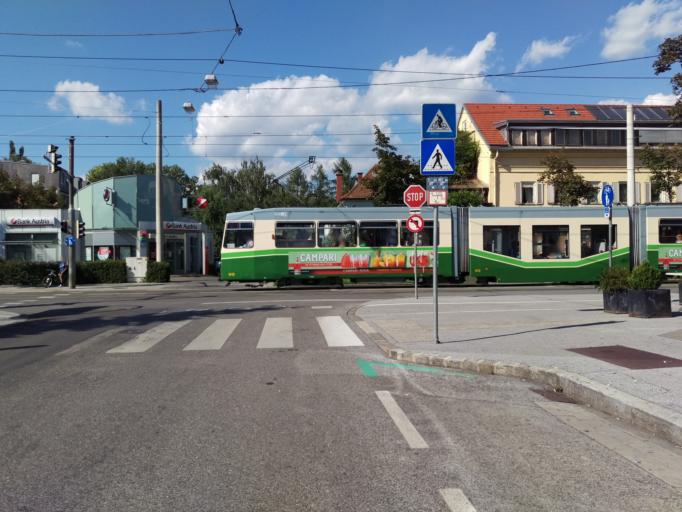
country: AT
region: Styria
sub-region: Graz Stadt
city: Wetzelsdorf
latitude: 47.0703
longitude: 15.4034
